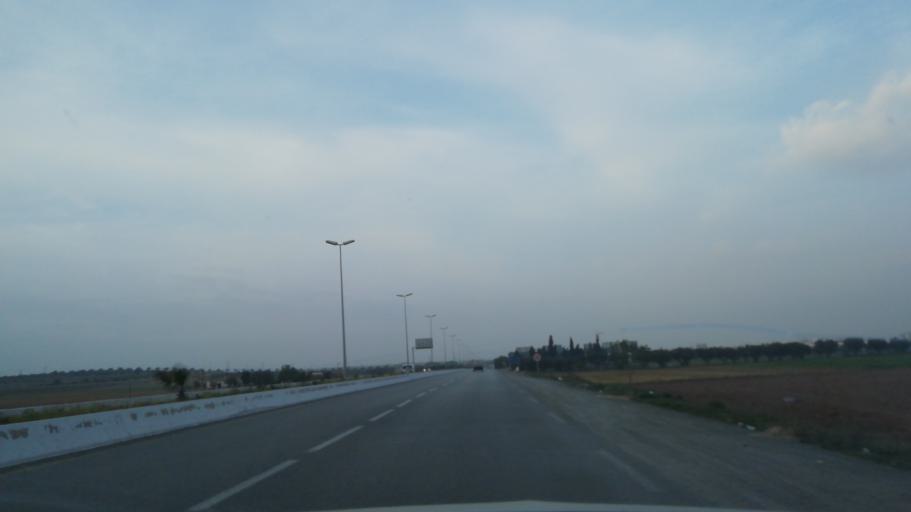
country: DZ
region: Sidi Bel Abbes
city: Sidi Bel Abbes
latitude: 35.1957
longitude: -0.6615
